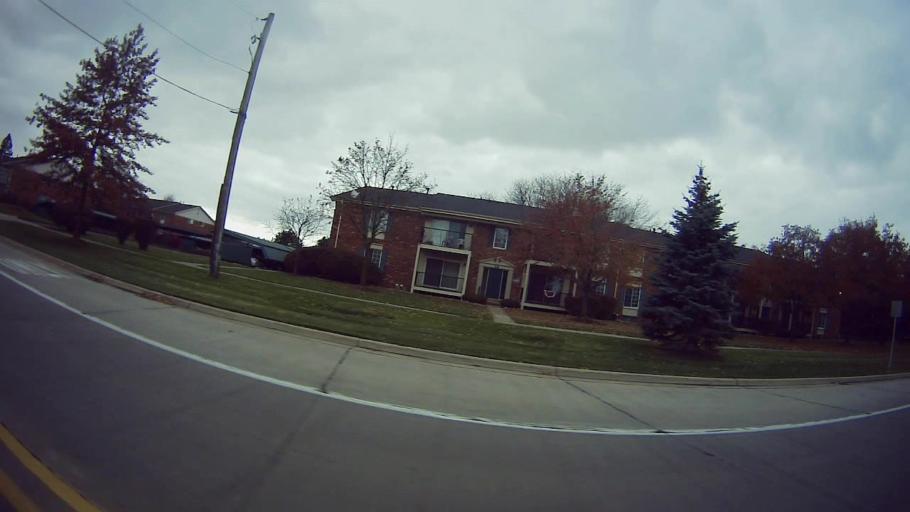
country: US
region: Michigan
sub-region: Macomb County
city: Sterling Heights
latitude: 42.5512
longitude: -83.0045
